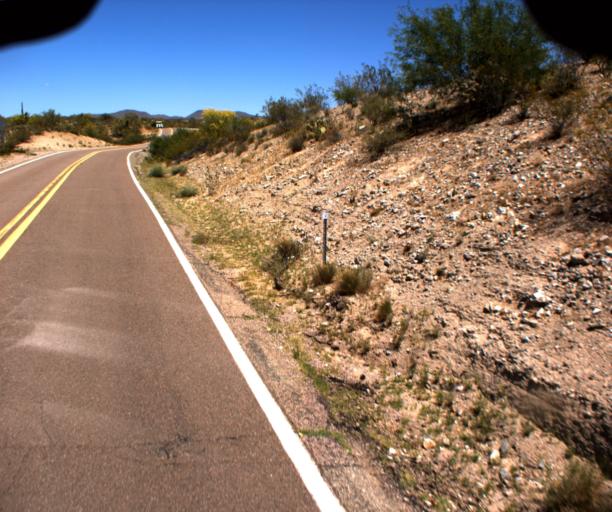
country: US
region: Arizona
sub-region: Yavapai County
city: Bagdad
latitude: 34.4479
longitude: -113.2428
